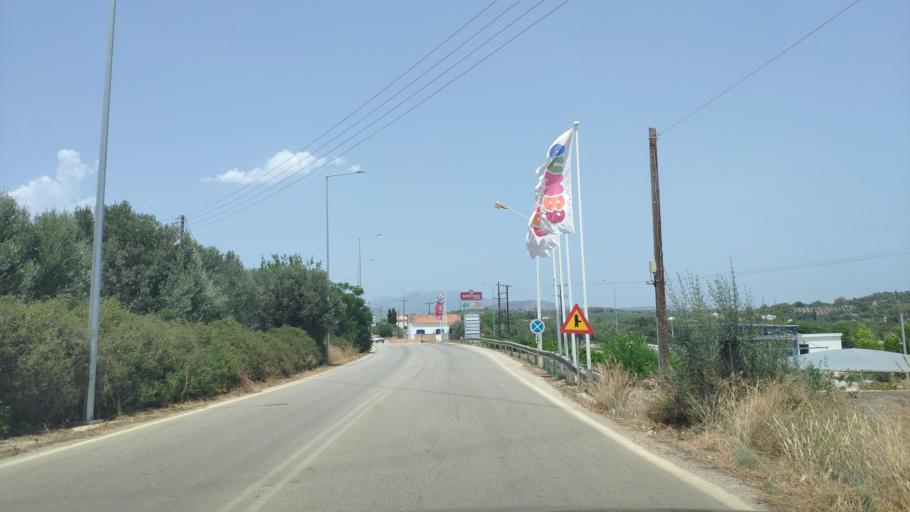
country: GR
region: Peloponnese
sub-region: Nomos Argolidos
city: Porto Cheli
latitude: 37.3418
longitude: 23.1573
